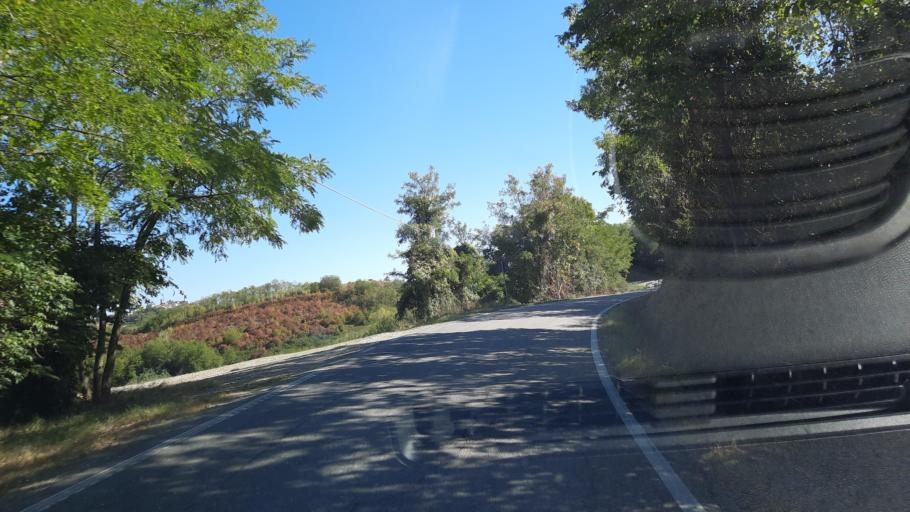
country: IT
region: Piedmont
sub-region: Provincia di Alessandria
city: Camagna Monferrato
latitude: 45.0284
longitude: 8.4350
